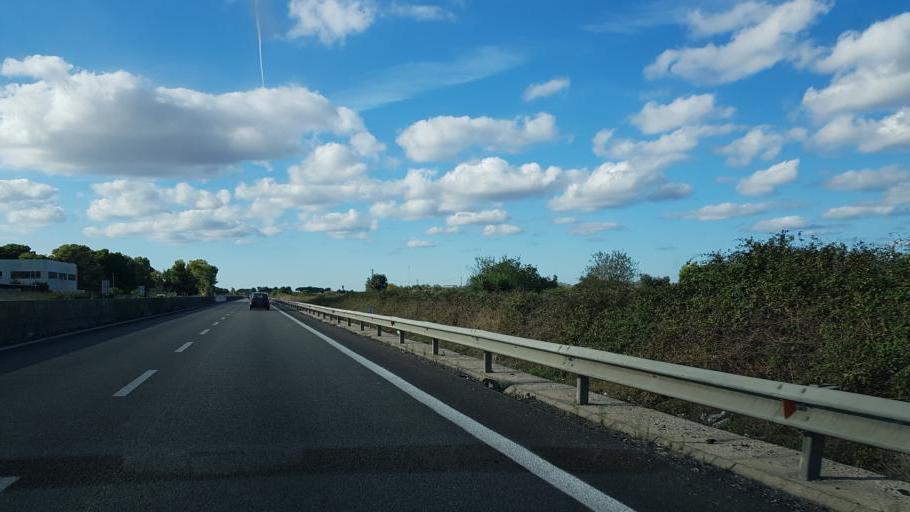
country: IT
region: Apulia
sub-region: Provincia di Lecce
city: Surbo
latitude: 40.3795
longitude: 18.1357
